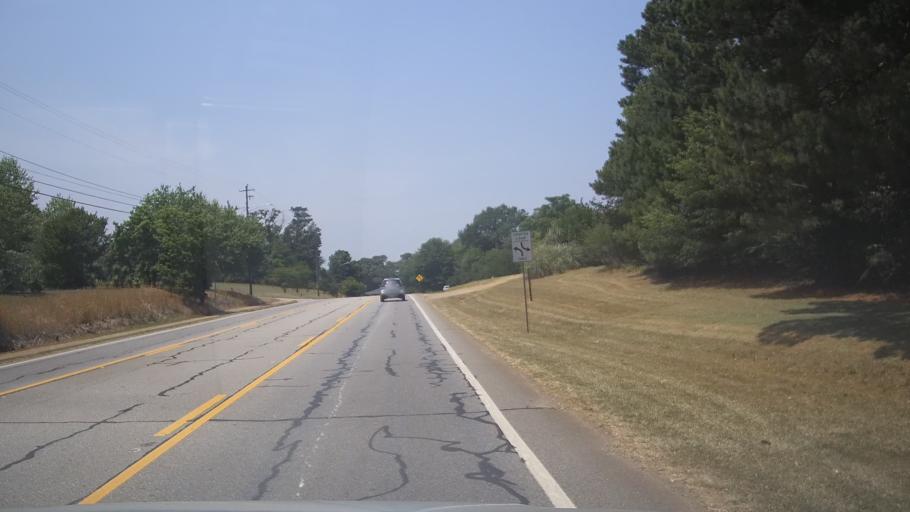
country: US
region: Georgia
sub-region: Hart County
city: Royston
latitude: 34.2855
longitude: -83.1409
